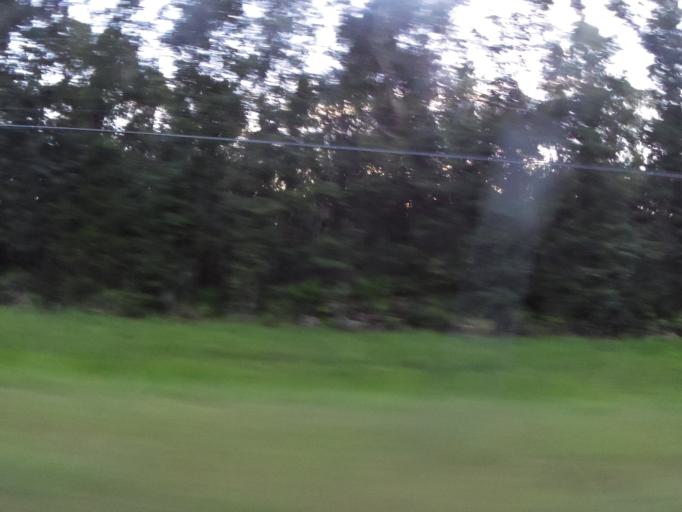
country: US
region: Georgia
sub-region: Camden County
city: Woodbine
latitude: 30.9447
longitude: -81.7190
